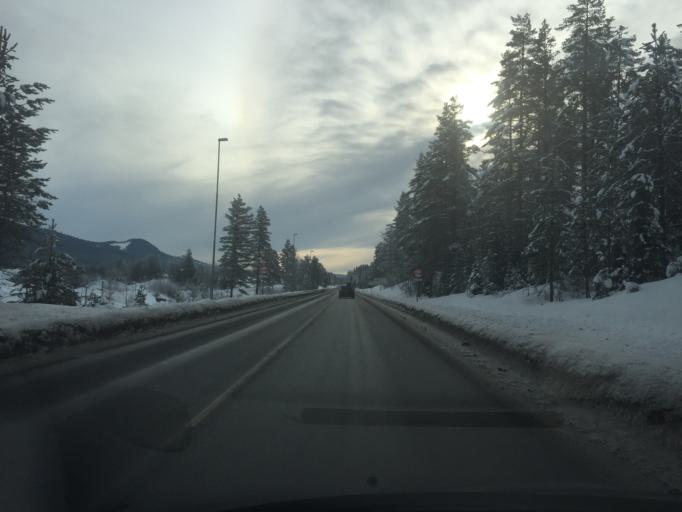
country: NO
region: Hedmark
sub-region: Trysil
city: Innbygda
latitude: 61.2994
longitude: 12.2640
